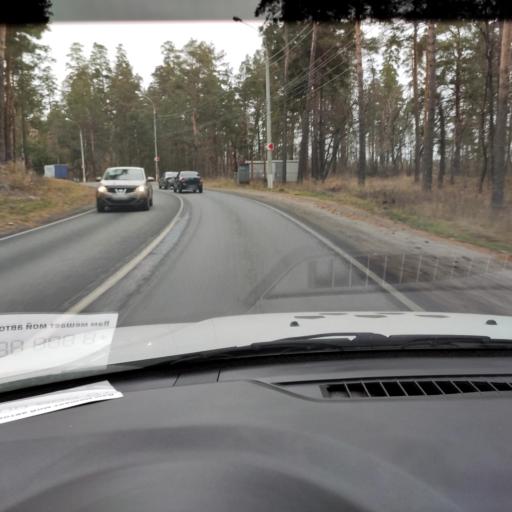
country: RU
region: Samara
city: Tol'yatti
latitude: 53.4874
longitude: 49.3110
